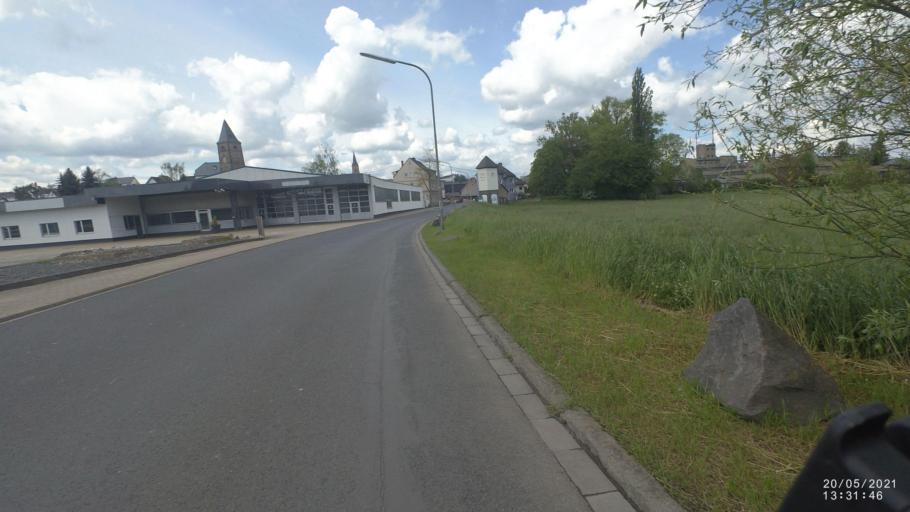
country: DE
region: Rheinland-Pfalz
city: Saffig
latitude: 50.3988
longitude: 7.4153
